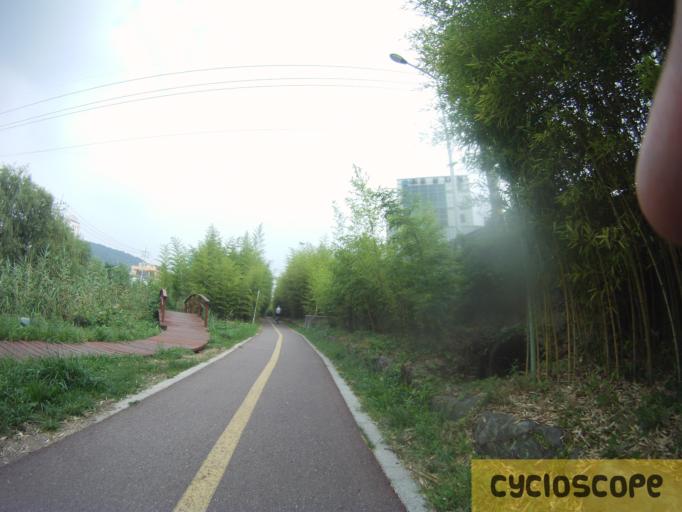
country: KR
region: Gyeonggi-do
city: Anyang-si
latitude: 37.3535
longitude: 126.9680
